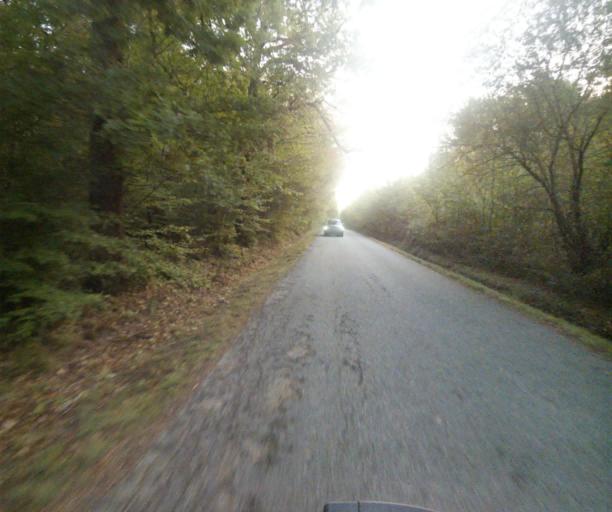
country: FR
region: Midi-Pyrenees
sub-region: Departement du Tarn-et-Garonne
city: Montech
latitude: 43.9421
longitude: 1.2809
